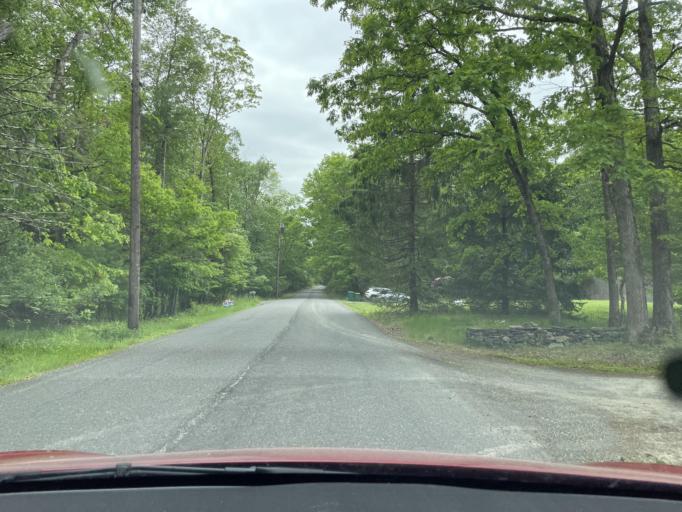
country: US
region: New York
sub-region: Ulster County
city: Zena
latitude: 41.9799
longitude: -74.0655
